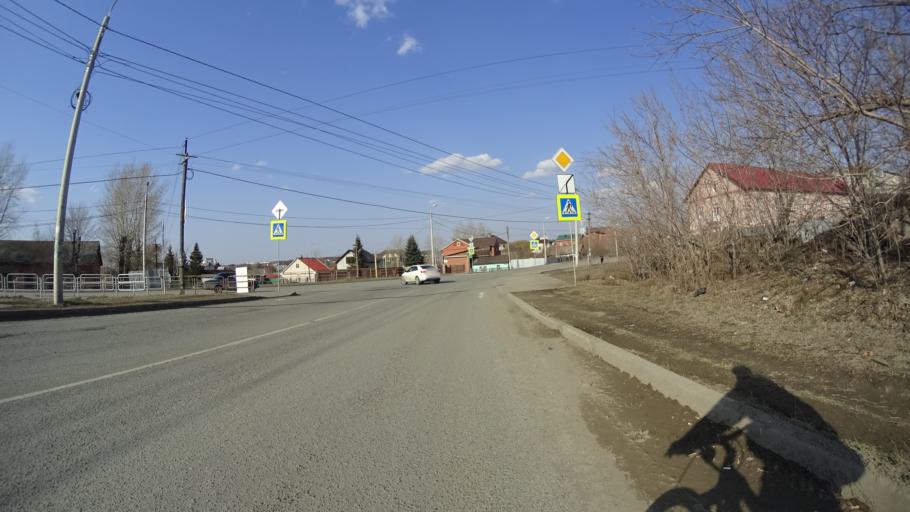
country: RU
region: Chelyabinsk
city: Novosineglazovskiy
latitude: 55.1114
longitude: 61.3326
